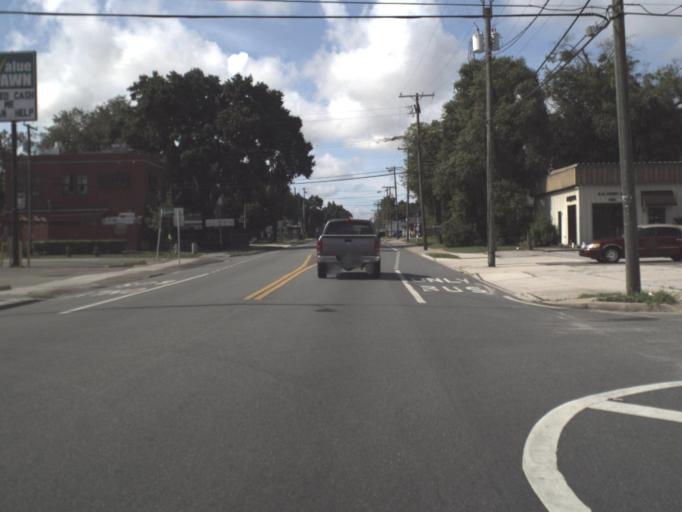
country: US
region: Florida
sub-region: Hillsborough County
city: Tampa
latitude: 27.9944
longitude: -82.4512
